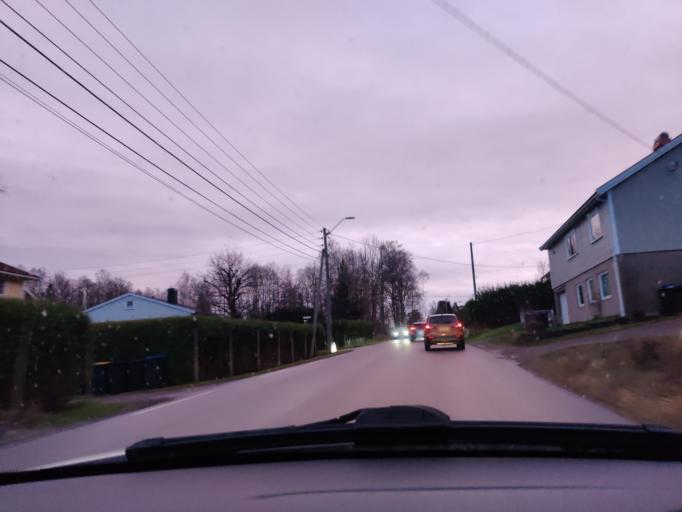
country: NO
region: Vestfold
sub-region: Tonsberg
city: Sem
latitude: 59.2692
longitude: 10.3658
